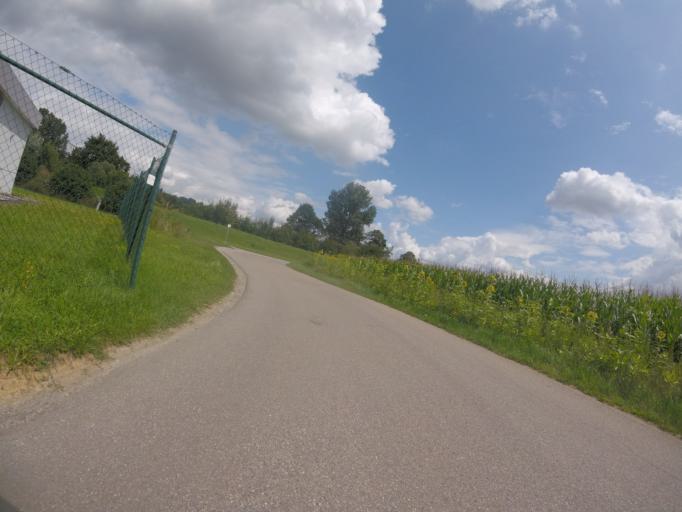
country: DE
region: Baden-Wuerttemberg
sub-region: Regierungsbezirk Stuttgart
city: Schorndorf
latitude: 48.8031
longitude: 9.5033
